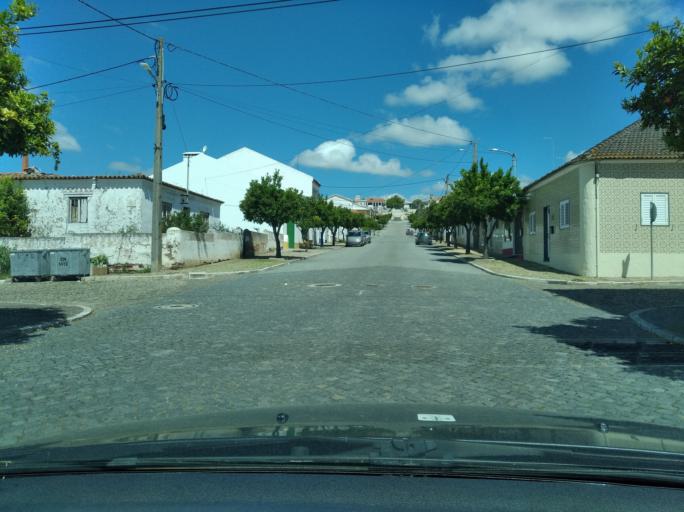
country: PT
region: Portalegre
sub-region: Avis
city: Avis
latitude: 39.0531
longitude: -7.8913
